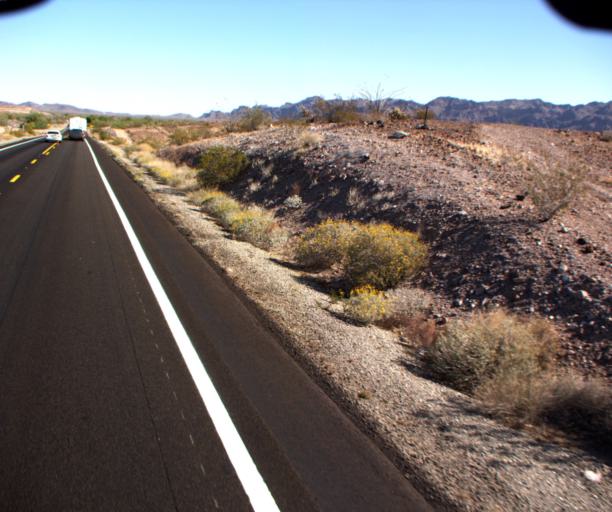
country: US
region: Arizona
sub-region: La Paz County
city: Quartzsite
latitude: 33.1609
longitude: -114.2796
